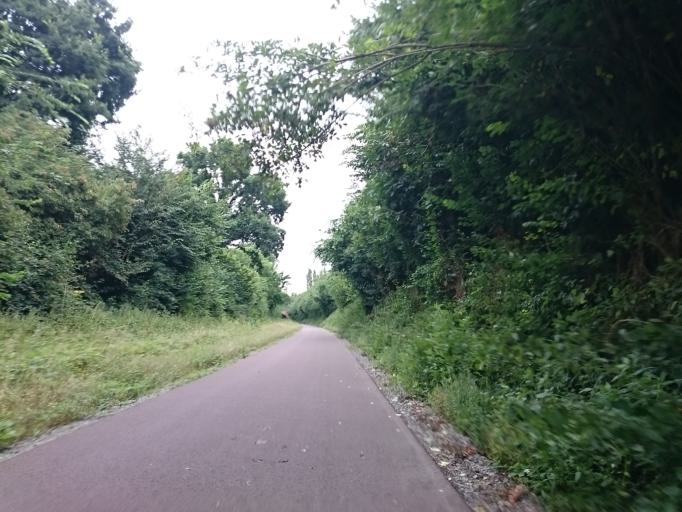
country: FR
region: Lower Normandy
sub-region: Departement du Calvados
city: Saint-Andre-sur-Orne
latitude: 49.1226
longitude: -0.3991
